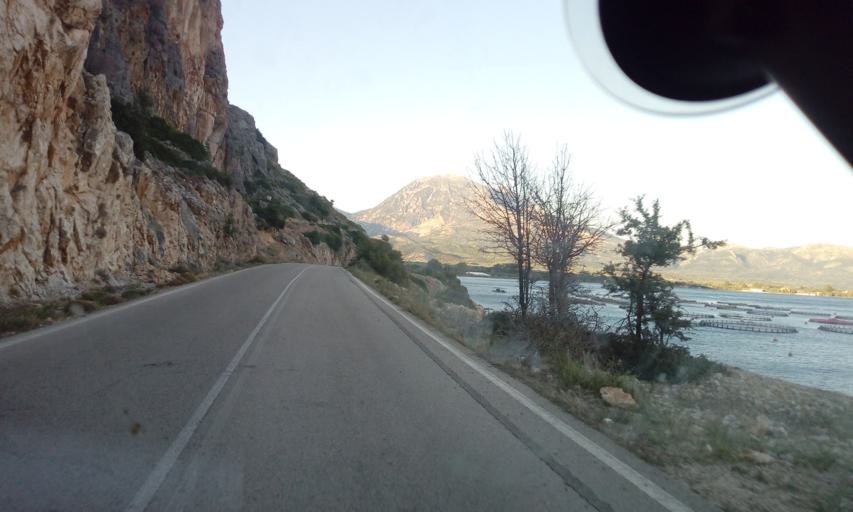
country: GR
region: West Greece
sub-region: Nomos Aitolias kai Akarnanias
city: Kandila
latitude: 38.6713
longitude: 20.9232
